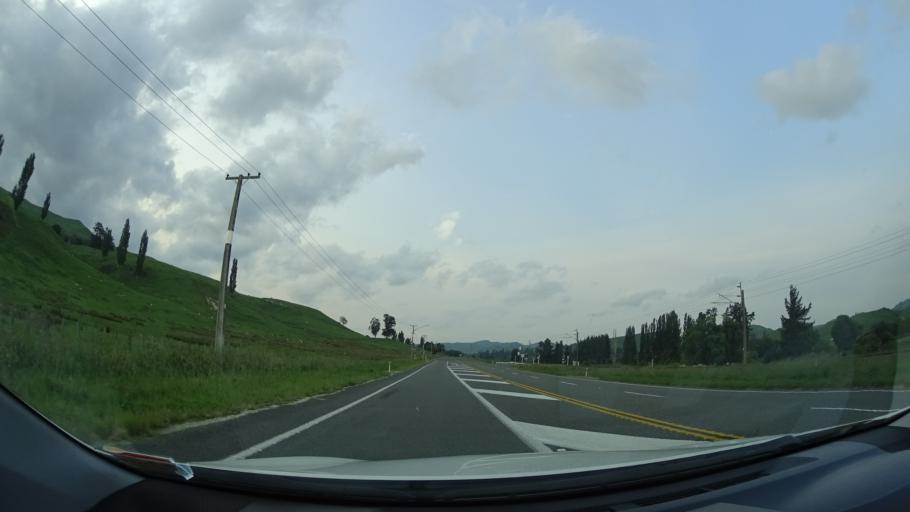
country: NZ
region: Manawatu-Wanganui
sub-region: Ruapehu District
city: Waiouru
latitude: -39.7202
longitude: 175.8407
